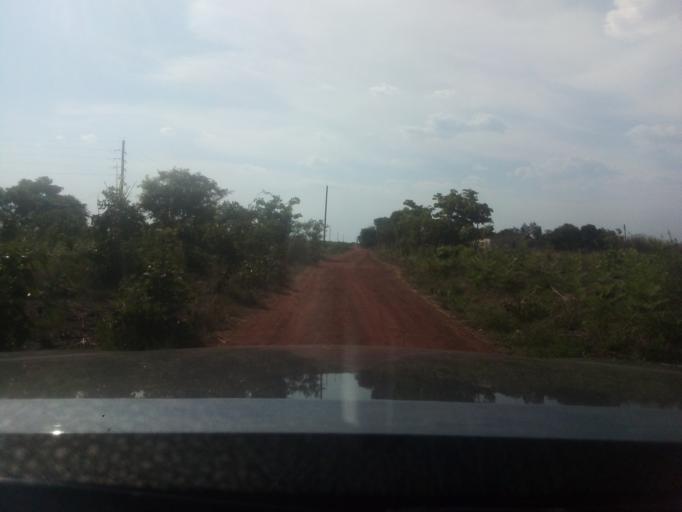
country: ZM
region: Northern
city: Kasama
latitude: -10.2155
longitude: 31.1406
